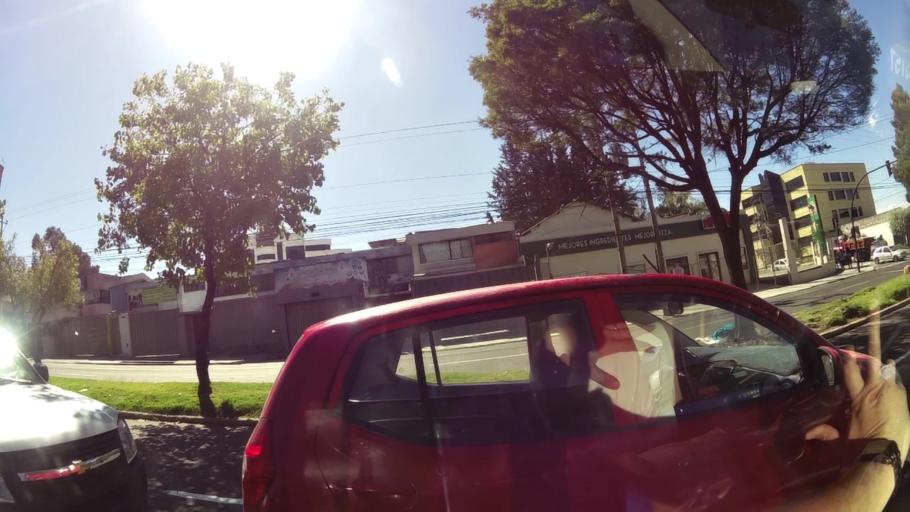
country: EC
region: Pichincha
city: Quito
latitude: -0.1439
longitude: -78.4696
